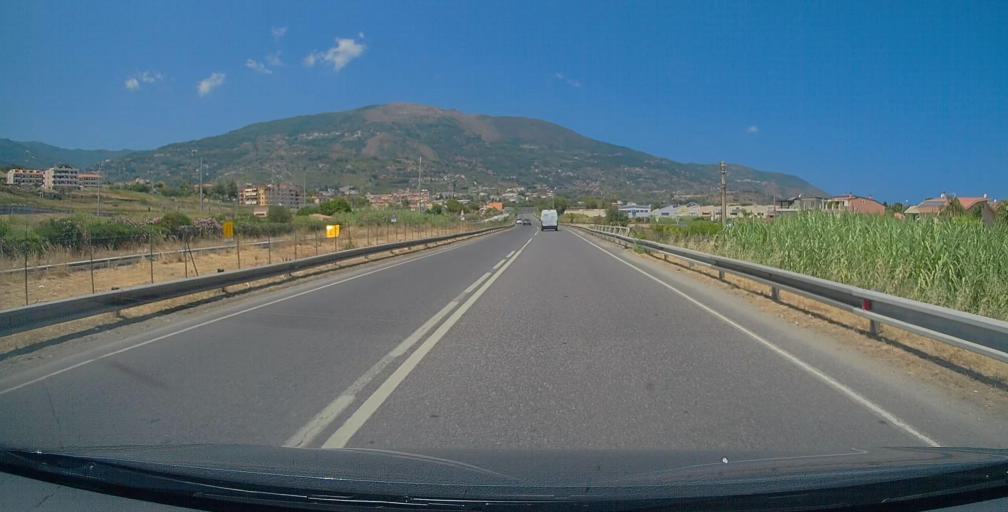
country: IT
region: Sicily
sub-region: Messina
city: Patti
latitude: 38.1466
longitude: 14.9831
